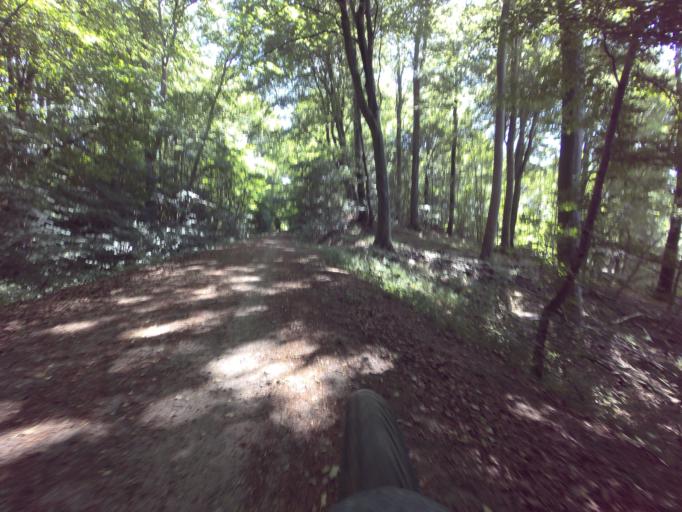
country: DK
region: Central Jutland
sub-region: Odder Kommune
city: Odder
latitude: 55.9316
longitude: 10.0826
